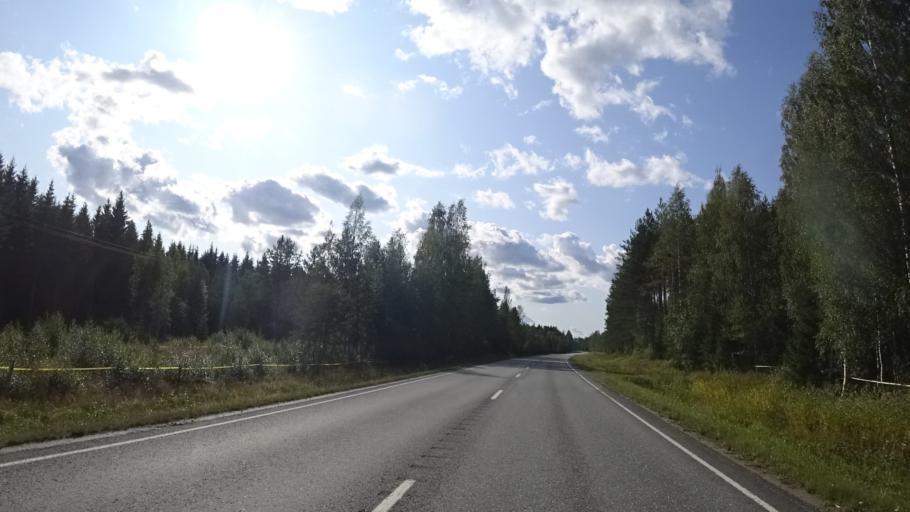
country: FI
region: North Karelia
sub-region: Keski-Karjala
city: Kitee
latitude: 62.0951
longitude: 30.0904
